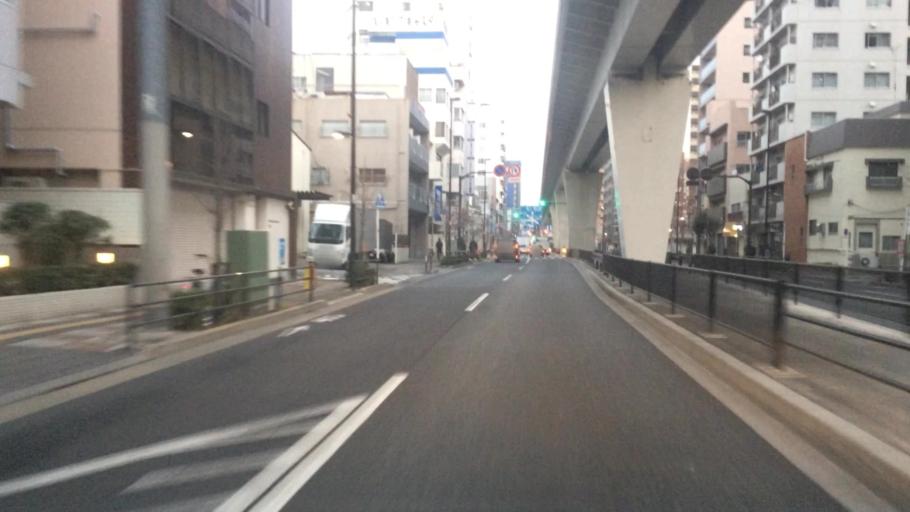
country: JP
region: Saitama
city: Kawaguchi
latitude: 35.7368
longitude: 139.7685
